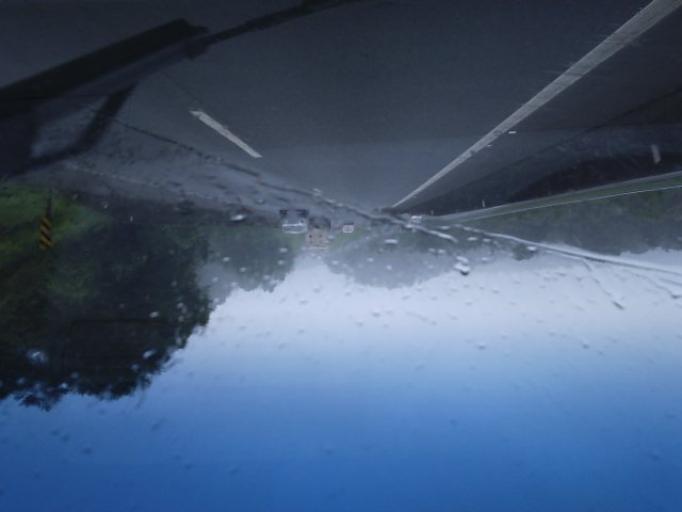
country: BR
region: Sao Paulo
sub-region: Cajati
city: Cajati
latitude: -24.9683
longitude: -48.3466
